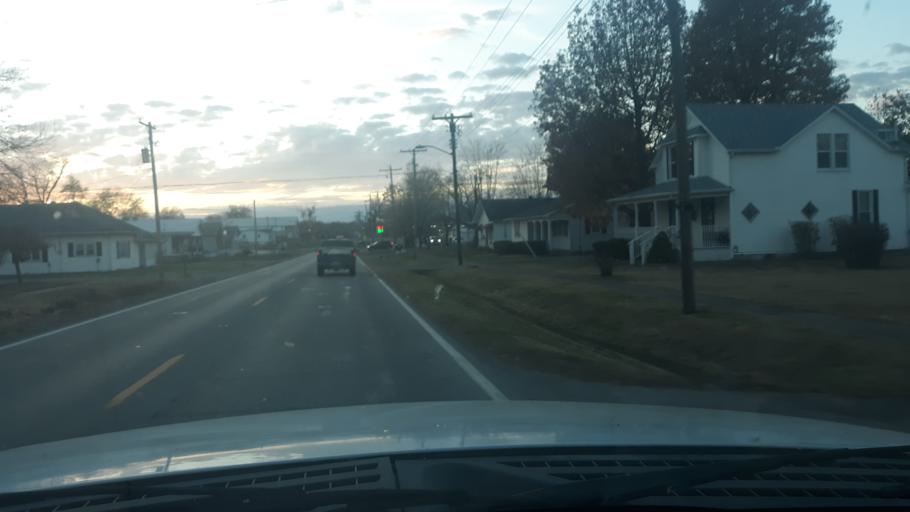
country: US
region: Illinois
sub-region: Saline County
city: Harrisburg
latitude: 37.8408
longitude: -88.6073
